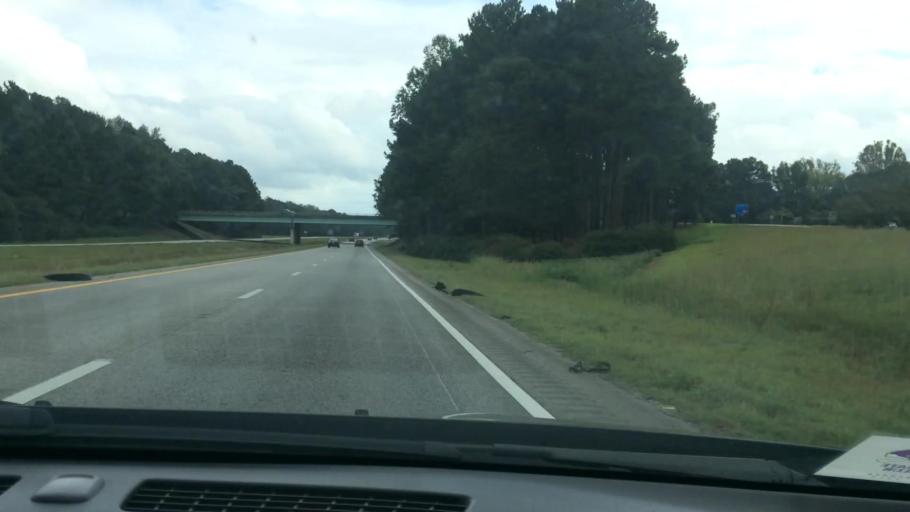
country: US
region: North Carolina
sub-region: Nash County
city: Spring Hope
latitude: 35.7875
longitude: -78.1194
